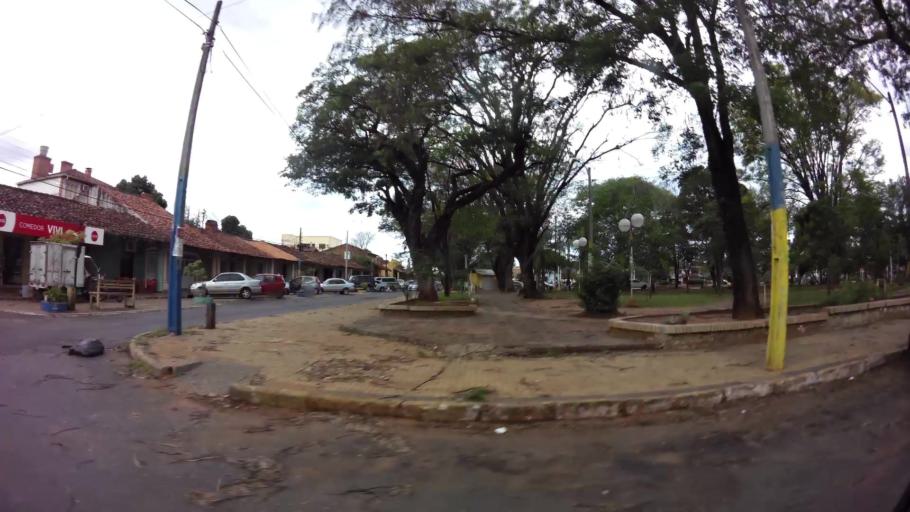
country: PY
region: Central
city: San Lorenzo
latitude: -25.2656
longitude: -57.4945
